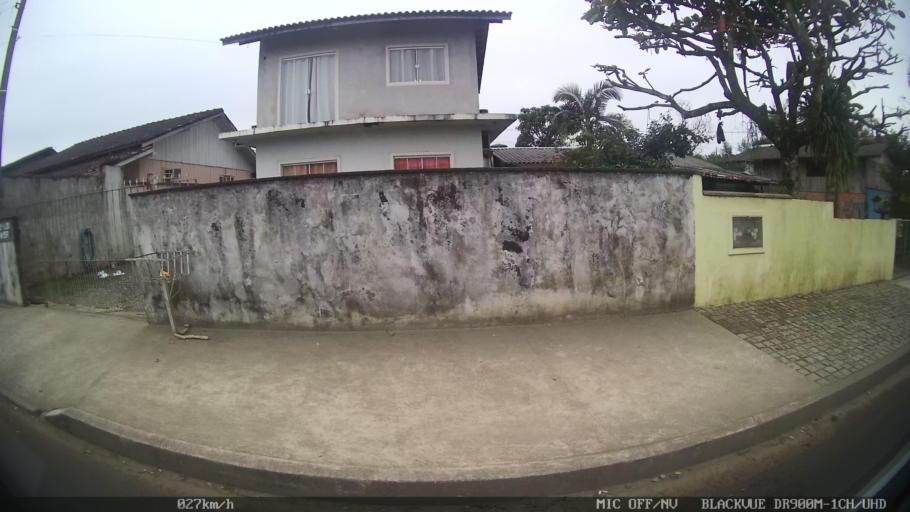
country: BR
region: Santa Catarina
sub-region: Joinville
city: Joinville
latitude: -26.2560
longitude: -48.8027
